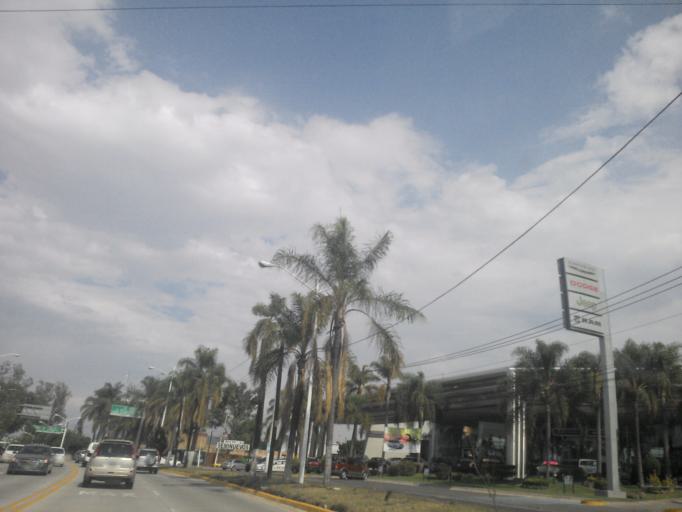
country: MX
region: Jalisco
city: Guadalajara
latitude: 20.6828
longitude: -103.4392
